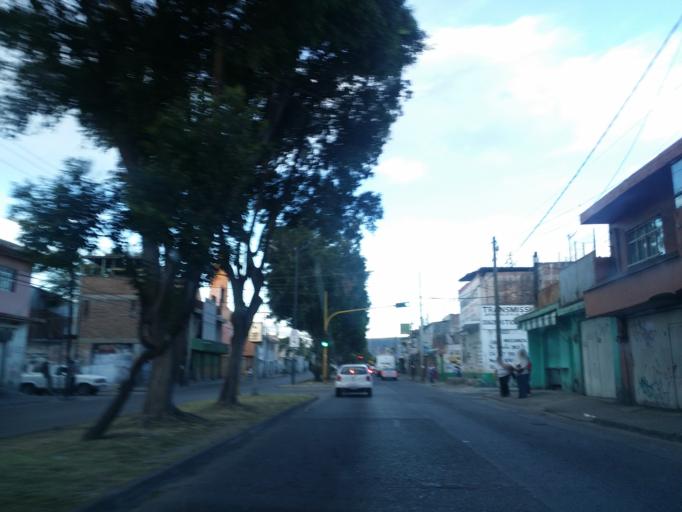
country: MX
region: Guanajuato
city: Leon
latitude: 21.1413
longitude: -101.6546
